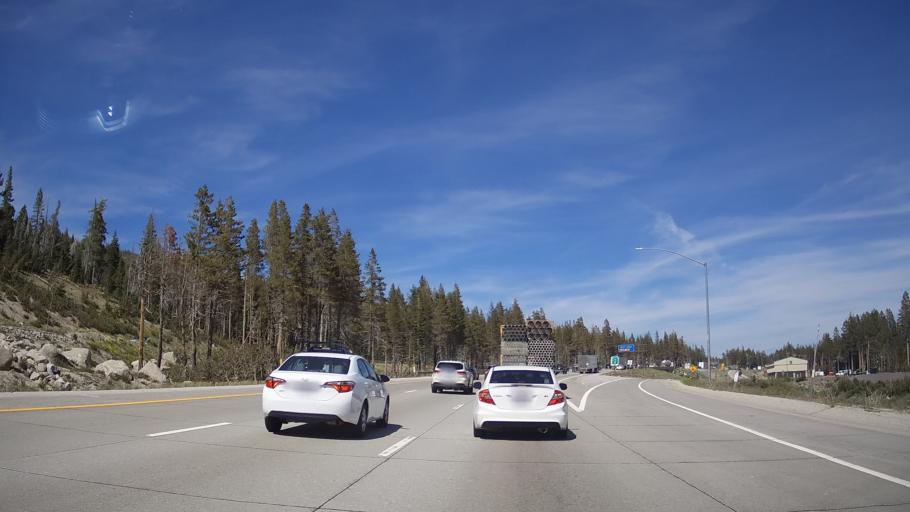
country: US
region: California
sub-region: Nevada County
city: Truckee
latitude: 39.3371
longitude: -120.3525
